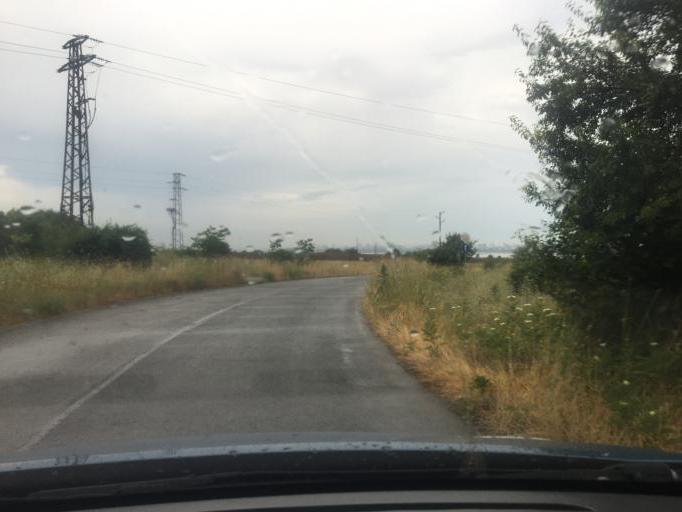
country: BG
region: Burgas
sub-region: Obshtina Burgas
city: Burgas
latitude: 42.5514
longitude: 27.4904
